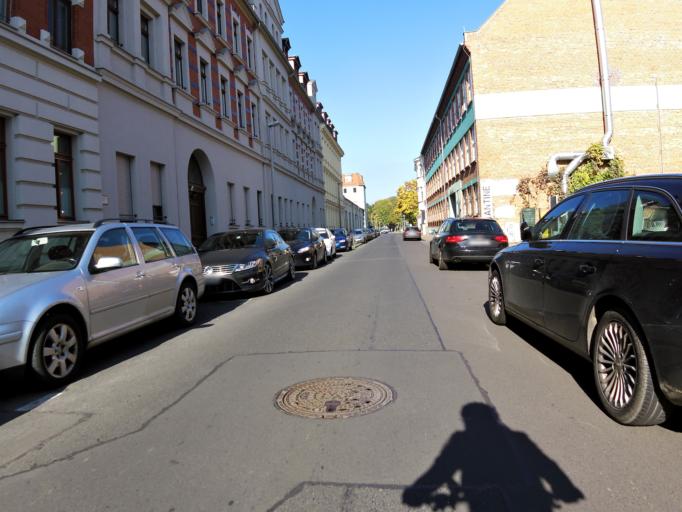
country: DE
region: Saxony
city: Leipzig
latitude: 51.3401
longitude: 12.3367
